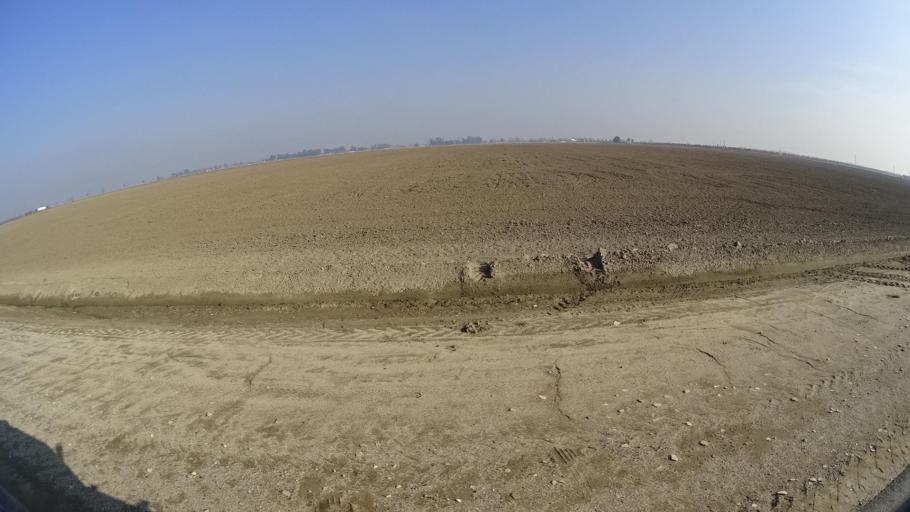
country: US
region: California
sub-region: Kern County
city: Greenfield
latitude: 35.2260
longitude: -119.0391
